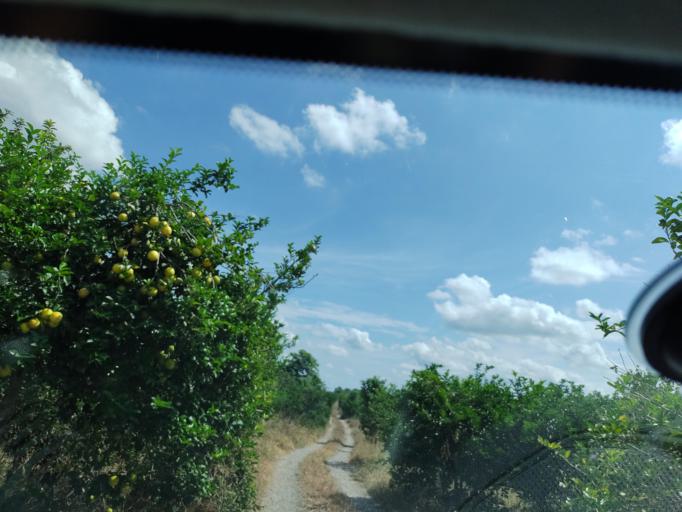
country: MX
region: Veracruz
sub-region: Martinez de la Torre
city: El Progreso
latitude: 20.1132
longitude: -97.0077
